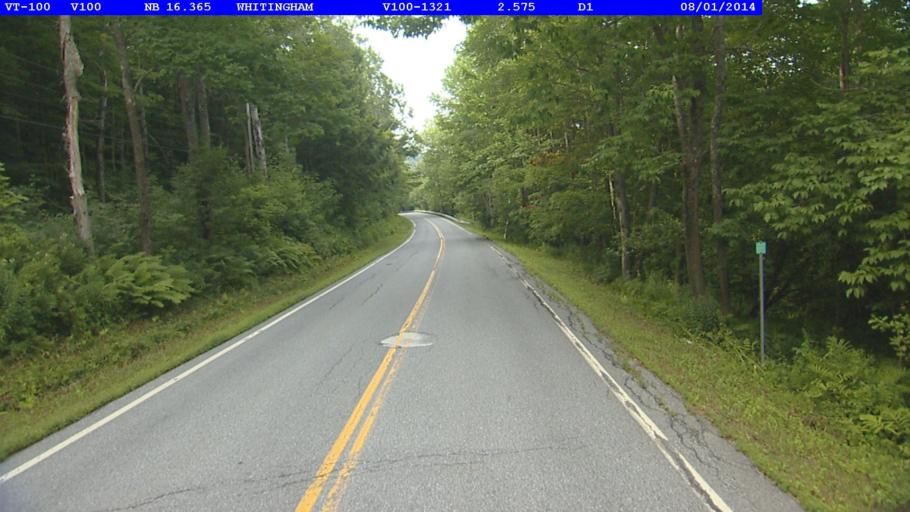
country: US
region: Massachusetts
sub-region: Franklin County
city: Charlemont
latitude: 42.7753
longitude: -72.8954
